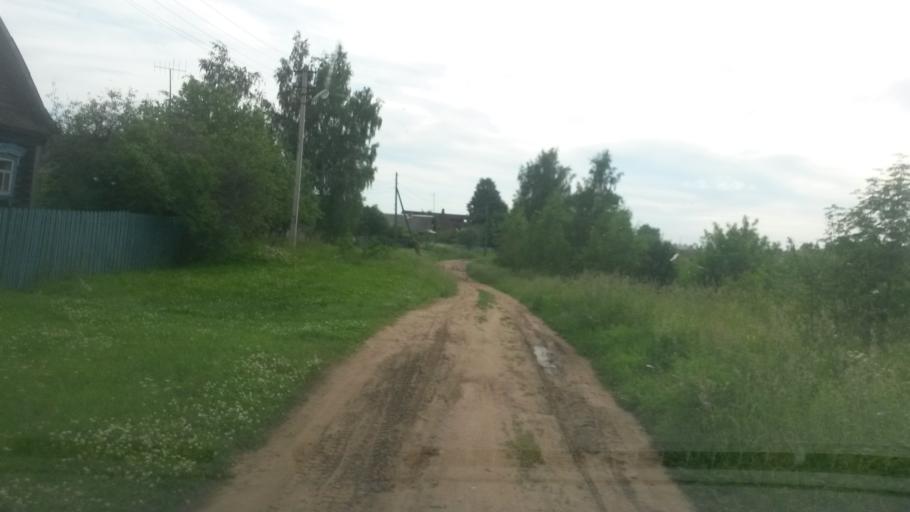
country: RU
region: Jaroslavl
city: Gavrilov-Yam
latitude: 57.3063
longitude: 39.9469
